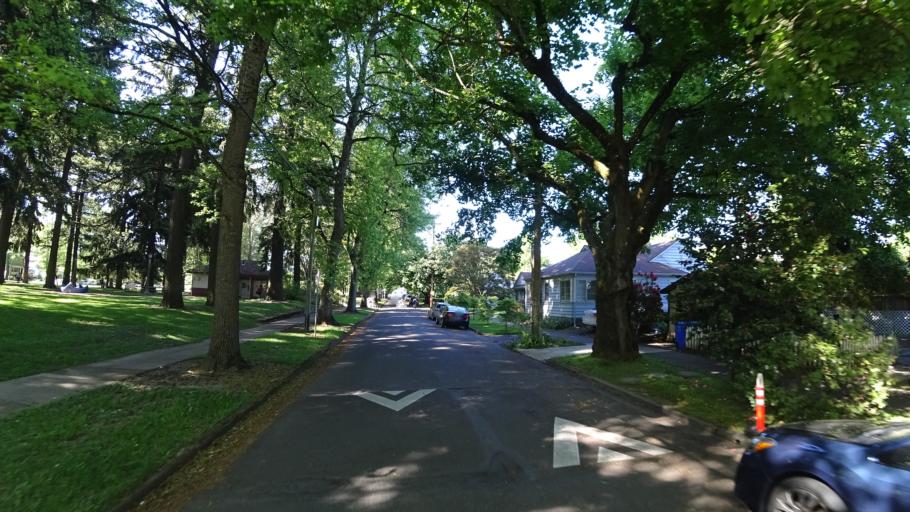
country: US
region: Oregon
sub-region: Multnomah County
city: Portland
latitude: 45.5274
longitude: -122.6345
